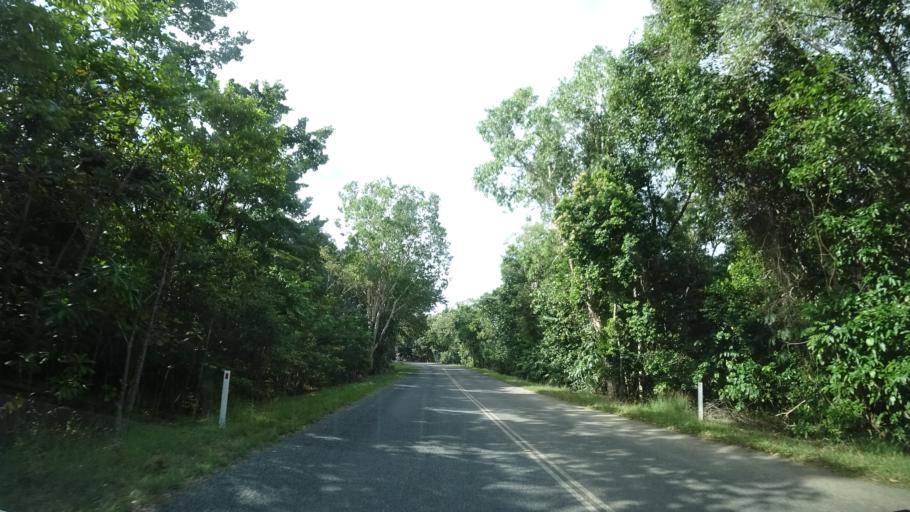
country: AU
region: Queensland
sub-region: Cairns
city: Port Douglas
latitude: -16.0915
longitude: 145.4608
